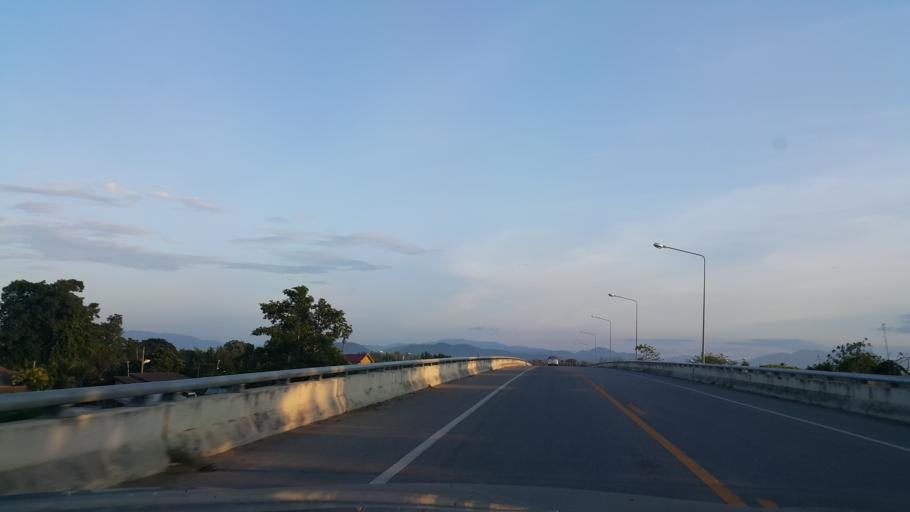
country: TH
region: Lamphun
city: Pa Sang
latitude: 18.5101
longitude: 98.8799
